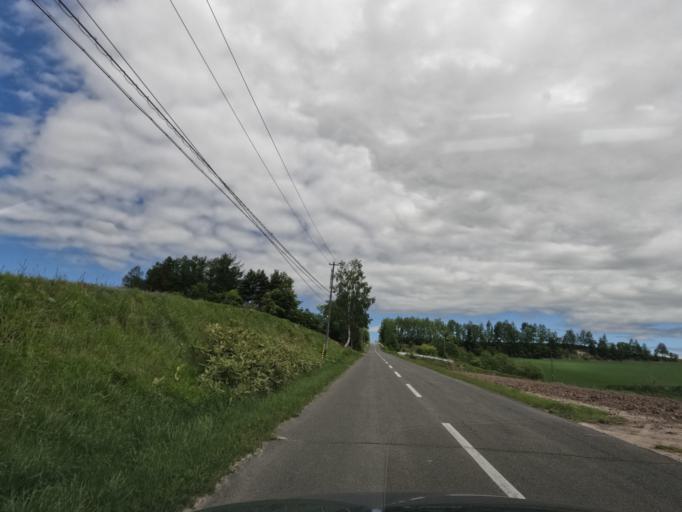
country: JP
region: Hokkaido
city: Shimo-furano
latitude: 43.5173
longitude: 142.4275
